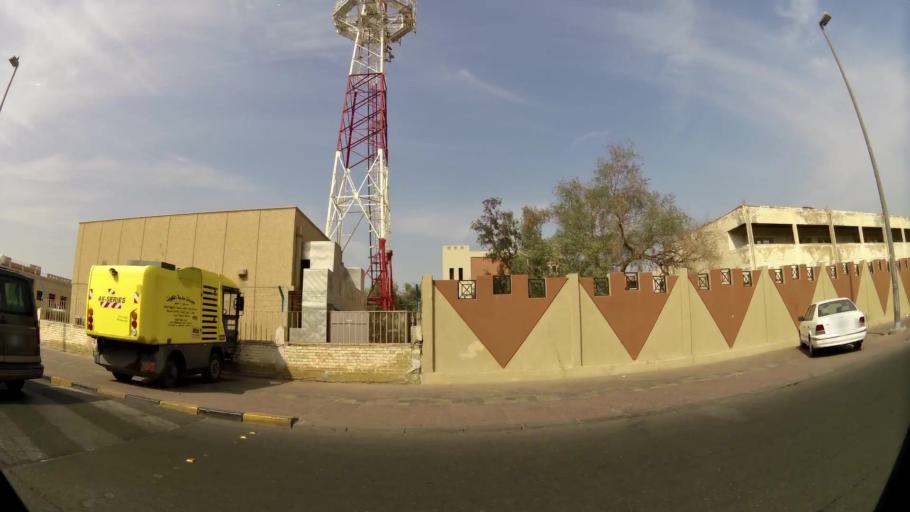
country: KW
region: Al Asimah
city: Ash Shamiyah
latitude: 29.3389
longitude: 47.9791
